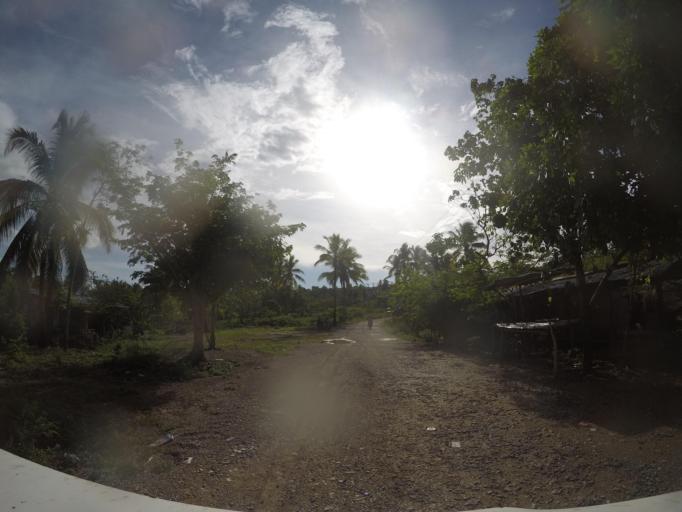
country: TL
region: Baucau
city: Baucau
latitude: -8.5086
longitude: 126.4444
